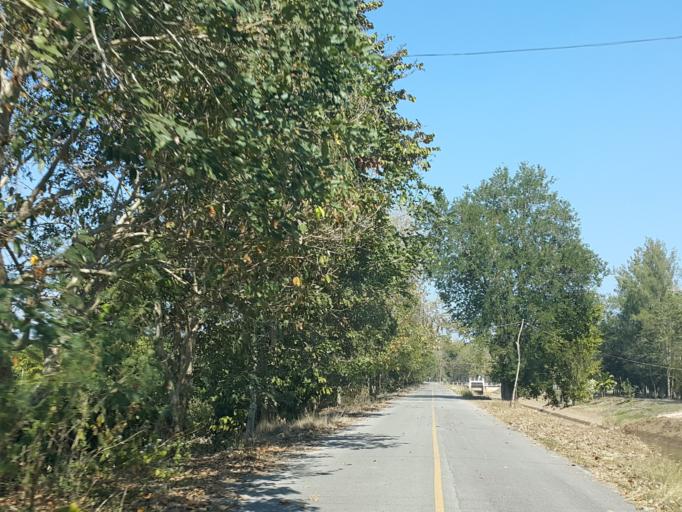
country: TH
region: Chiang Mai
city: Mae Taeng
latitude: 19.0947
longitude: 98.9514
